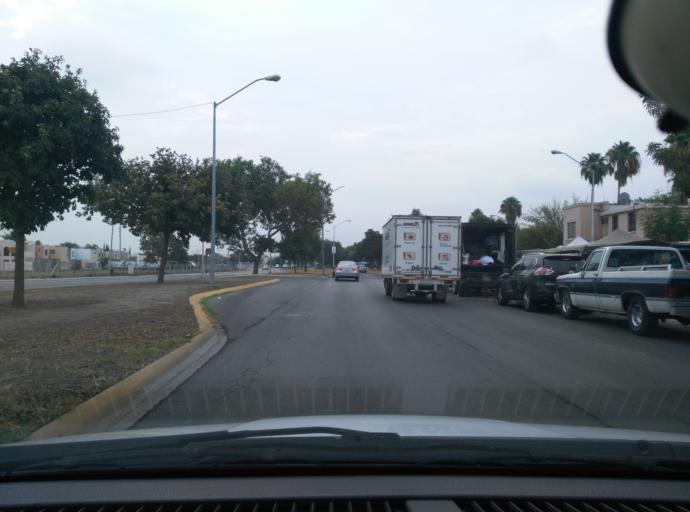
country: MX
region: Nuevo Leon
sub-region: Apodaca
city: Fraccionamiento Cosmopolis Octavo Sector
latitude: 25.7719
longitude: -100.2556
